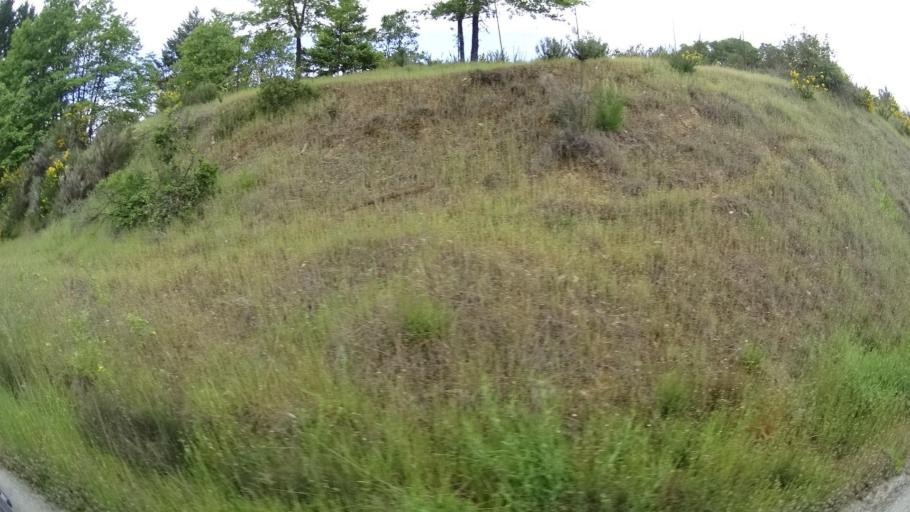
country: US
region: California
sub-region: Humboldt County
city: Redway
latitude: 40.1054
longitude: -123.7868
